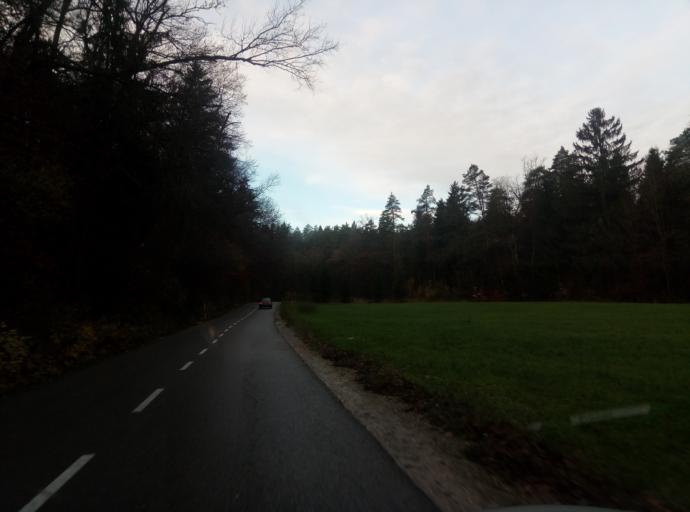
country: SI
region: Menges
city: Menges
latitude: 46.1713
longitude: 14.5550
